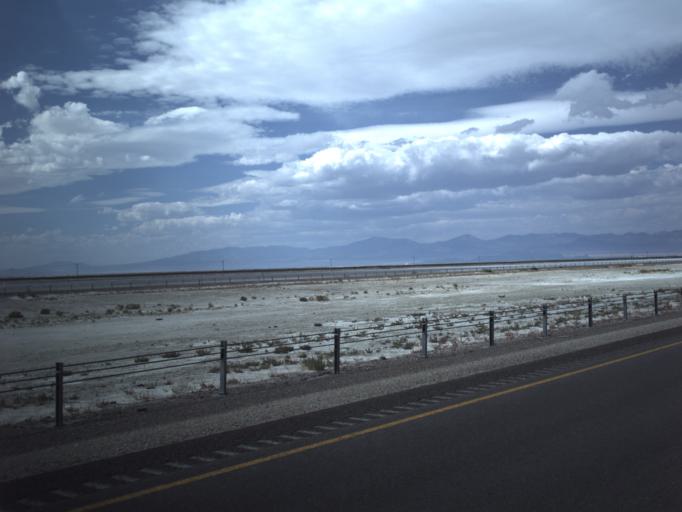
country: US
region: Utah
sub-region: Tooele County
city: Wendover
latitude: 40.7389
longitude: -113.8241
